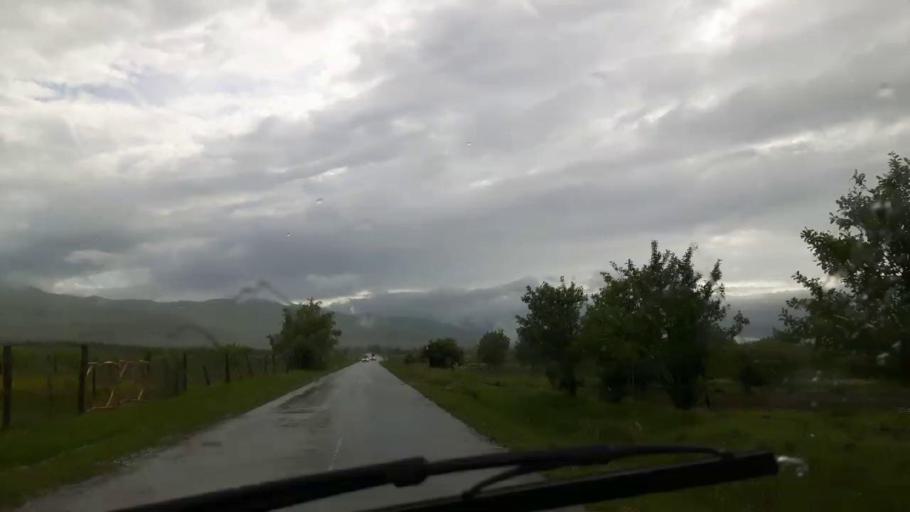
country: GE
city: Agara
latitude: 42.0012
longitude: 43.7544
